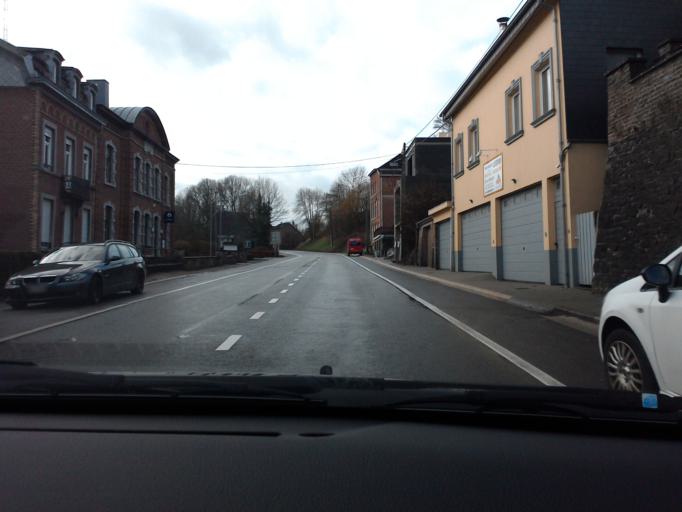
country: BE
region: Wallonia
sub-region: Province de Liege
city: Stavelot
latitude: 50.3910
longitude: 5.9244
